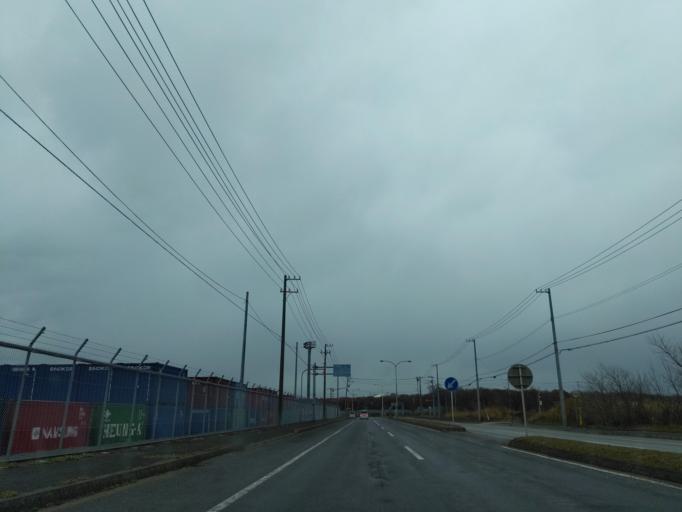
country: JP
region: Hokkaido
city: Ishikari
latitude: 43.1918
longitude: 141.2947
